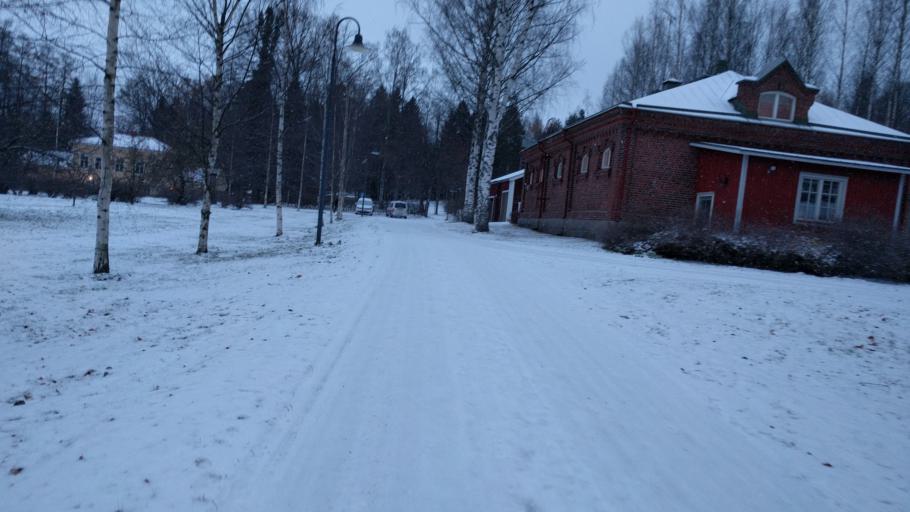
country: FI
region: Paijanne Tavastia
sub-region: Lahti
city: Heinola
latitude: 61.1674
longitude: 25.9867
